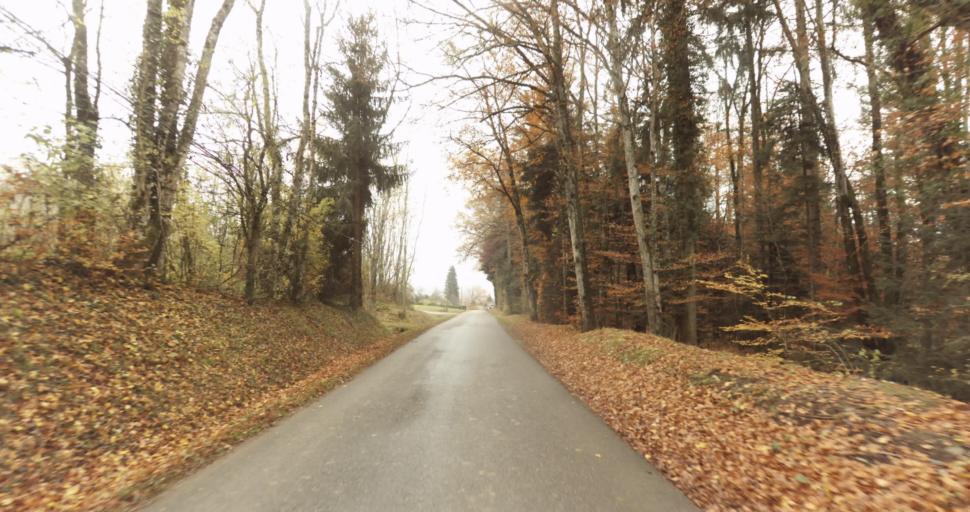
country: FR
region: Rhone-Alpes
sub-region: Departement de la Haute-Savoie
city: Groisy
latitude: 46.0314
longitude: 6.1934
